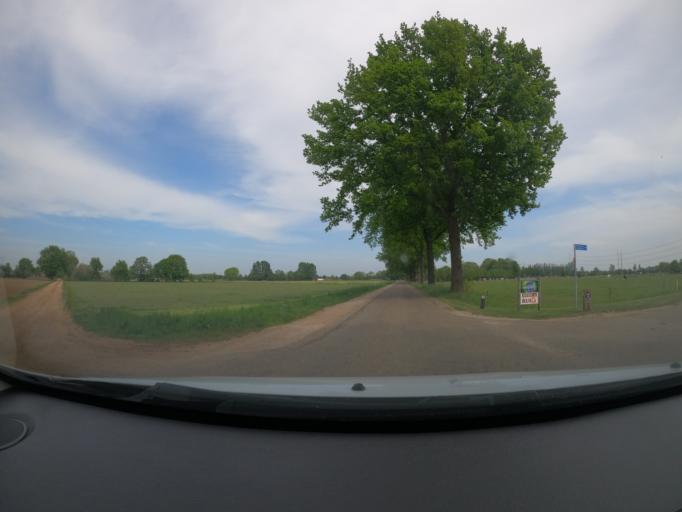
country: NL
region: Gelderland
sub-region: Oude IJsselstreek
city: Wisch
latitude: 51.9016
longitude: 6.3981
